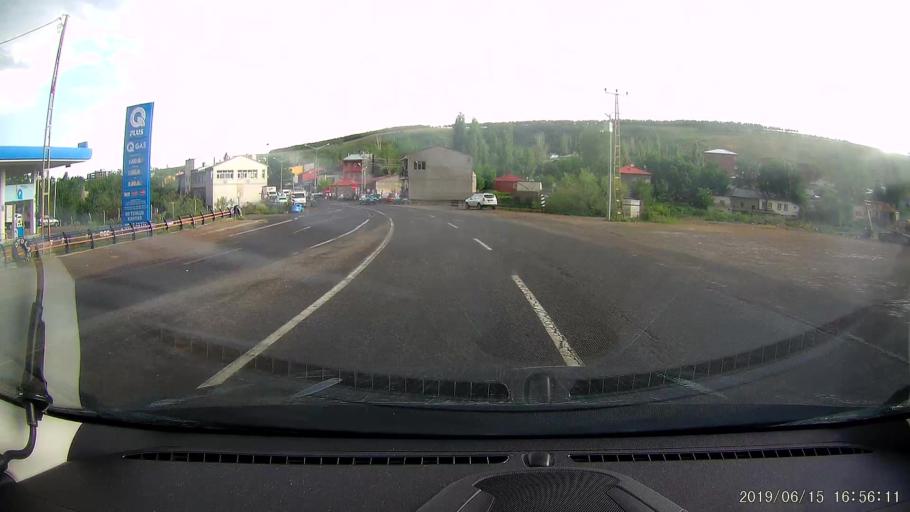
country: TR
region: Kars
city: Susuz
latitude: 40.7813
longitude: 43.1269
